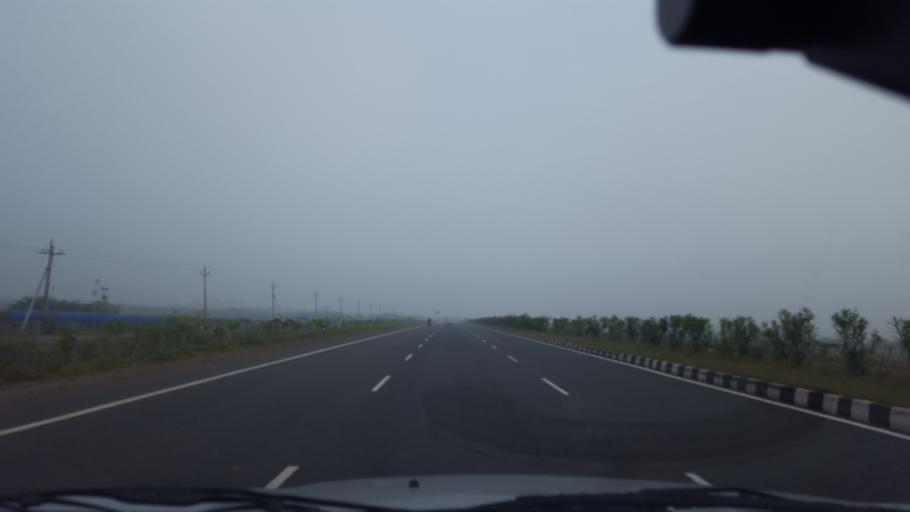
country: IN
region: Andhra Pradesh
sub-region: Prakasam
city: Ongole
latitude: 15.4875
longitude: 80.0640
